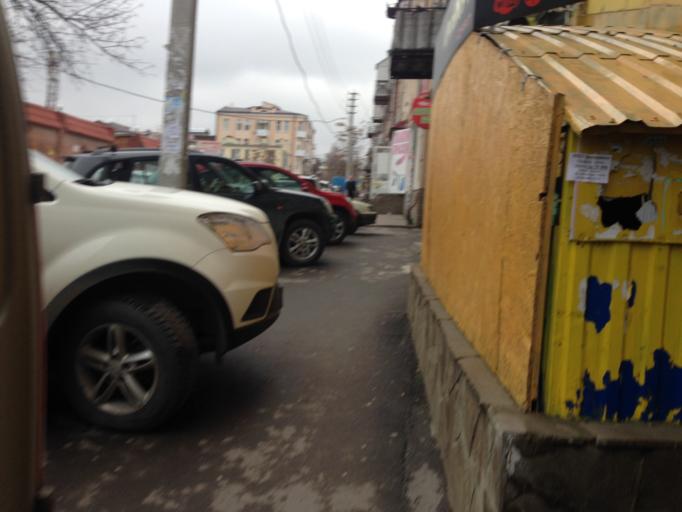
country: RU
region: Rostov
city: Rostov-na-Donu
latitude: 47.2167
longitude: 39.7132
